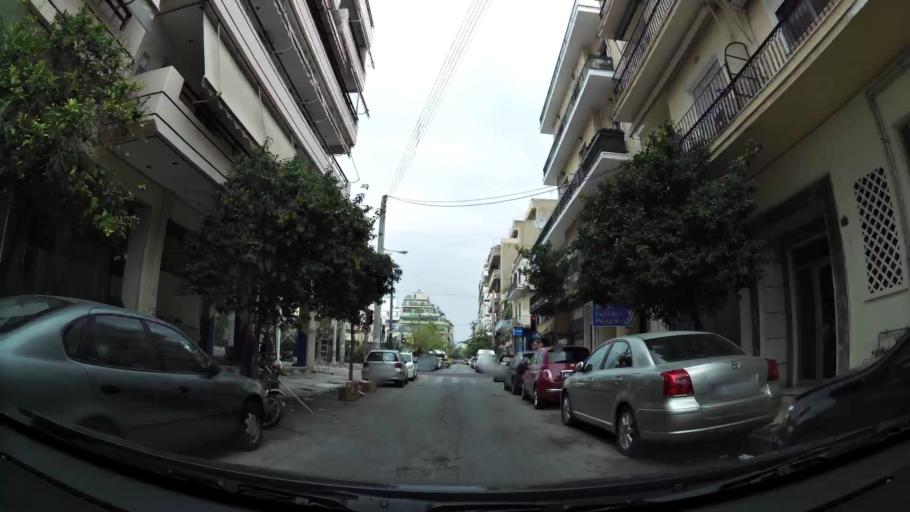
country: GR
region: Attica
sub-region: Nomarchia Athinas
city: Moskhaton
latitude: 37.9435
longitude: 23.6597
